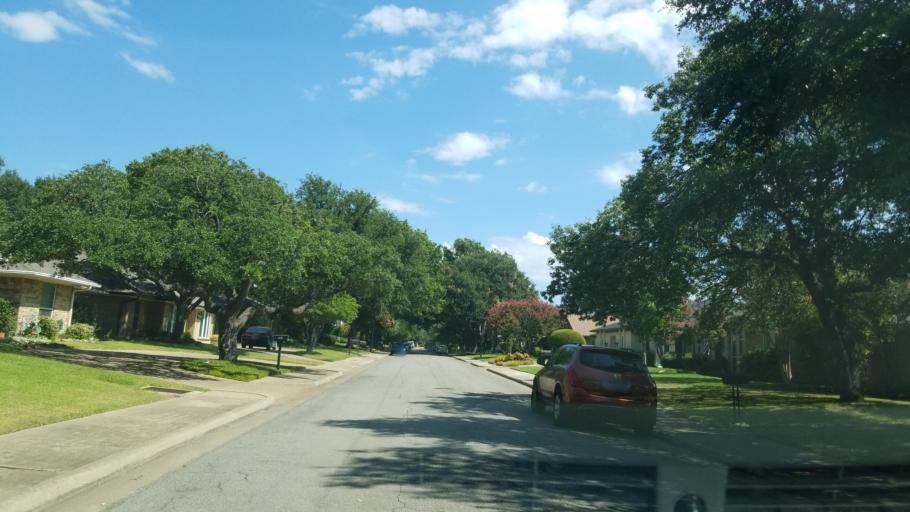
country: US
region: Texas
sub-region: Dallas County
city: Addison
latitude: 32.9695
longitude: -96.7889
